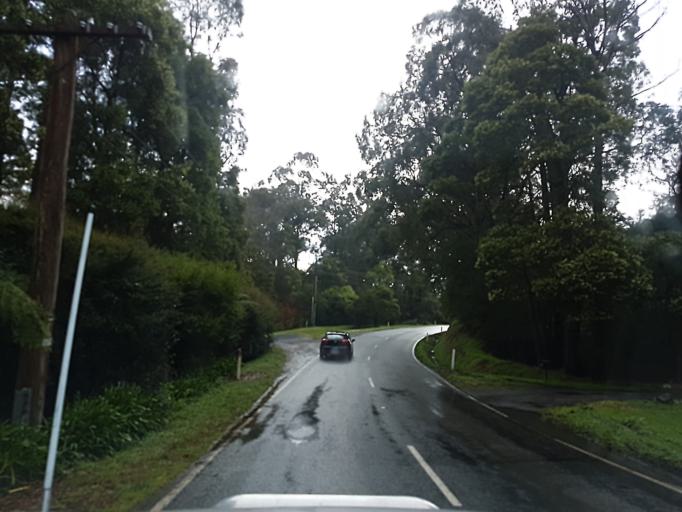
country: AU
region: Victoria
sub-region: Yarra Ranges
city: Millgrove
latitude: -37.7360
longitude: 145.7410
